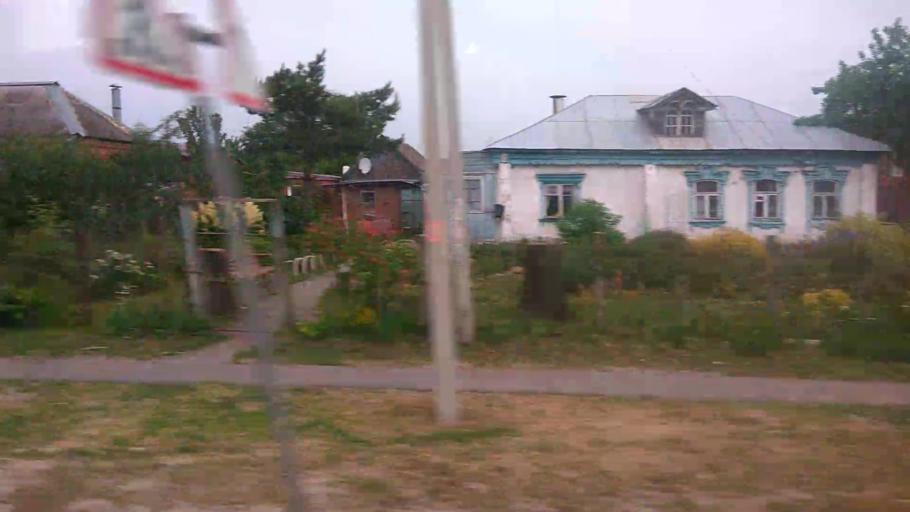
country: RU
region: Moskovskaya
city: Lukhovitsy
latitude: 54.9336
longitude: 39.0057
